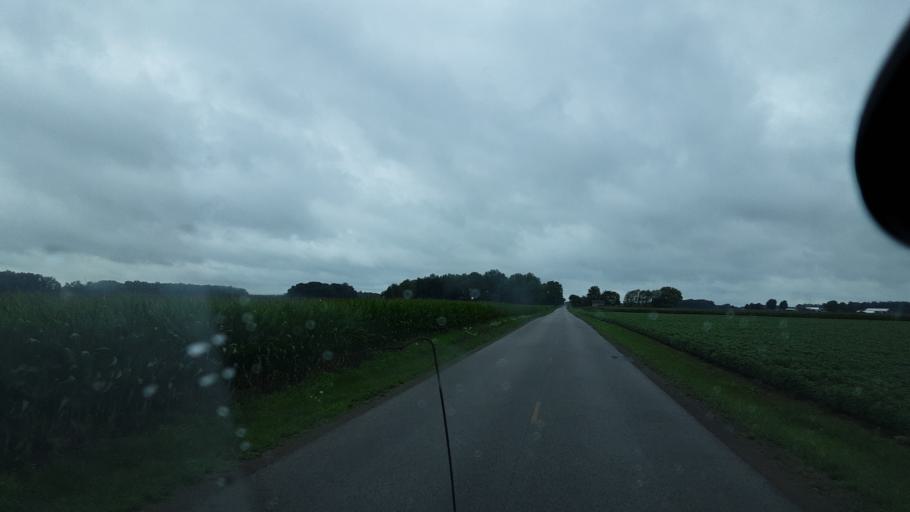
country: US
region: Ohio
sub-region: Van Wert County
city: Van Wert
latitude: 40.8004
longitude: -84.6690
